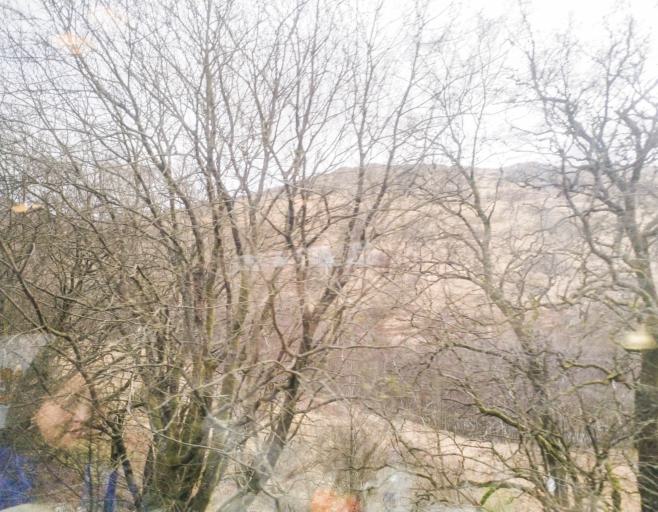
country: GB
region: Scotland
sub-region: Argyll and Bute
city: Garelochhead
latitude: 56.3515
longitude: -4.6928
